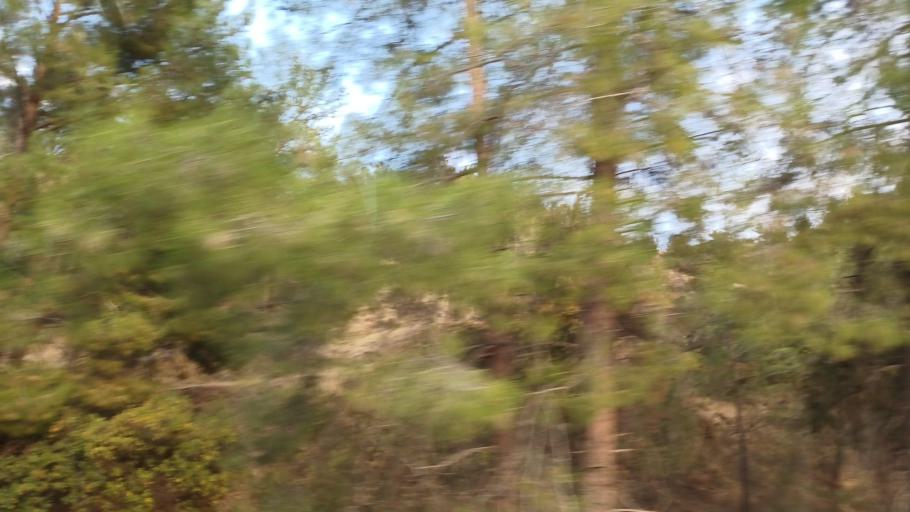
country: CY
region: Lefkosia
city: Kakopetria
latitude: 35.0275
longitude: 32.9010
